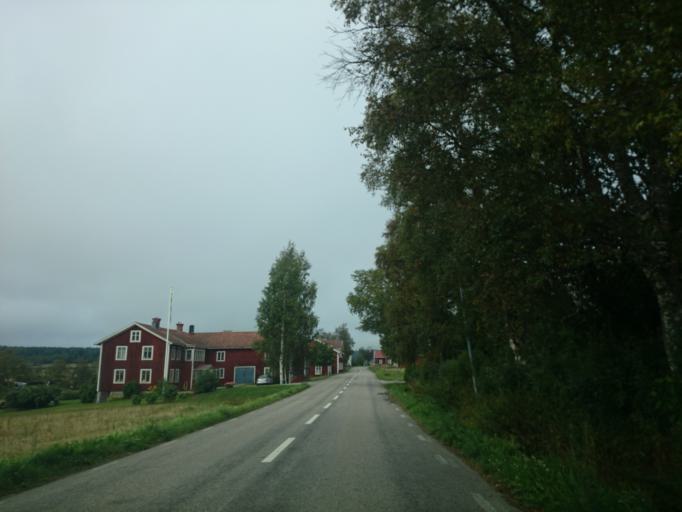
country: SE
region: Gaevleborg
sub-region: Nordanstigs Kommun
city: Bergsjoe
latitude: 61.9735
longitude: 17.2577
